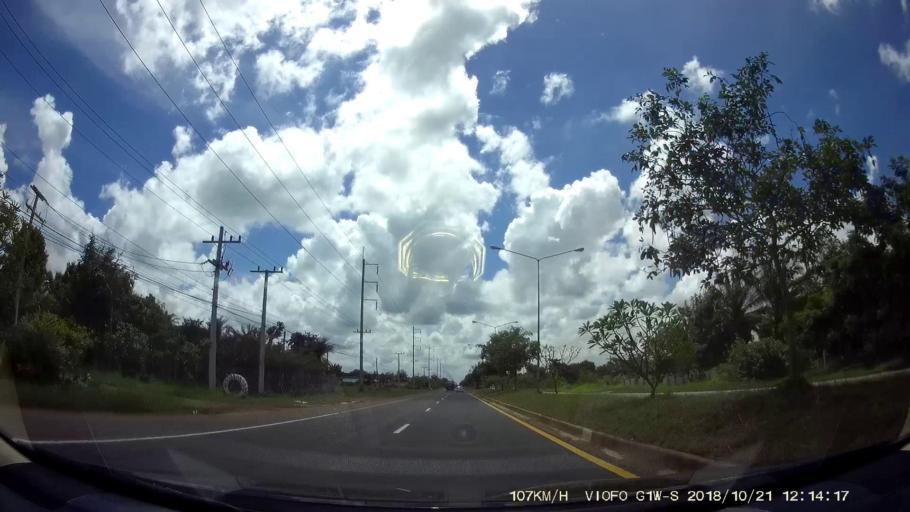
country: TH
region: Nakhon Ratchasima
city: Dan Khun Thot
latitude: 15.3797
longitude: 101.8359
